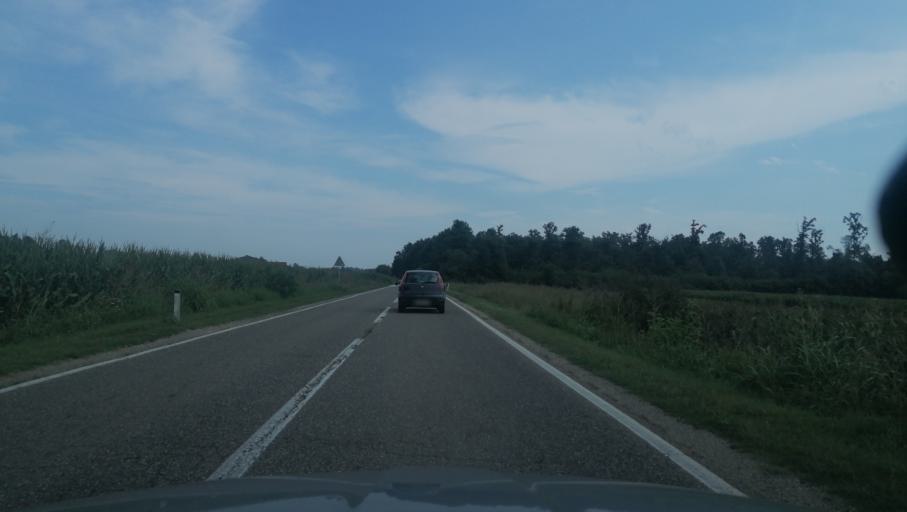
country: HR
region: Vukovarsko-Srijemska
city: Soljani
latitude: 44.8307
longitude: 19.0018
